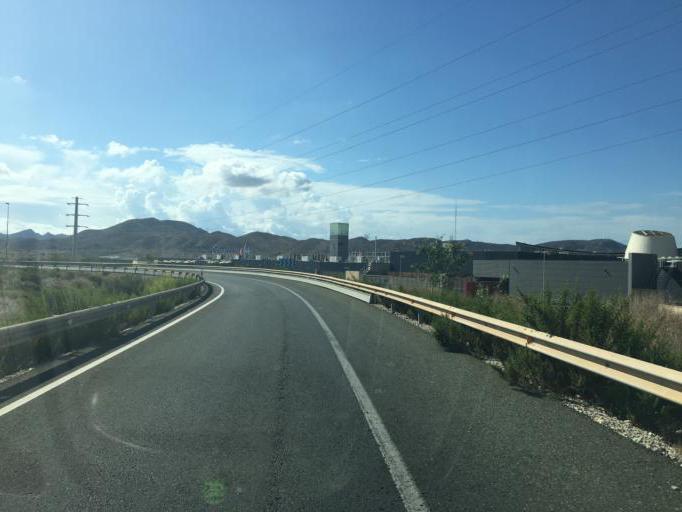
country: ES
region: Murcia
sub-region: Murcia
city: Cartagena
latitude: 37.6277
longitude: -0.9485
